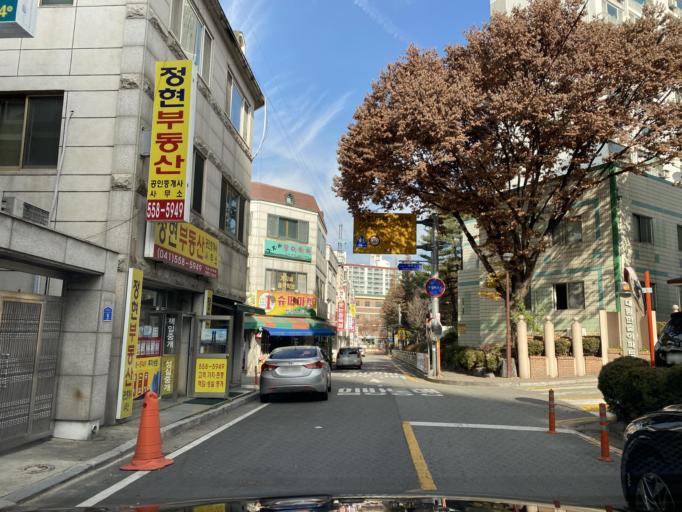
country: KR
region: Chungcheongnam-do
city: Cheonan
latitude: 36.8207
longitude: 127.1601
